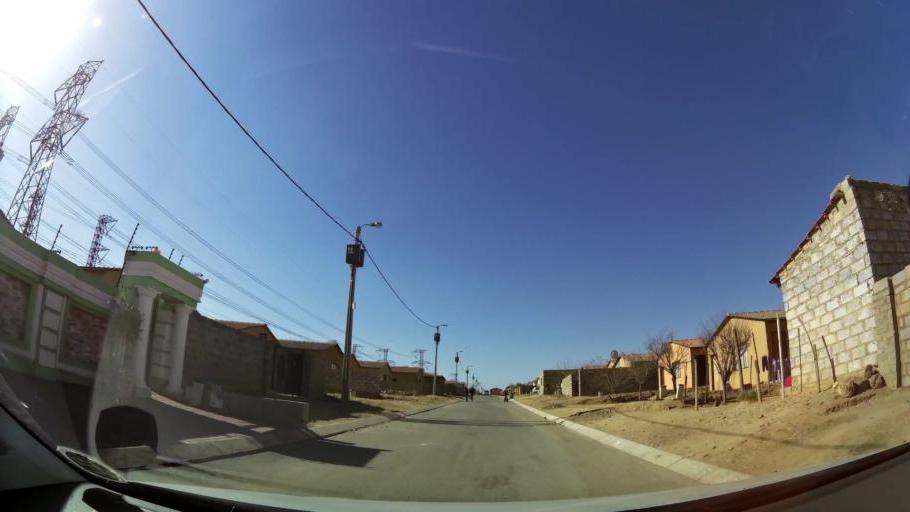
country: ZA
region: Gauteng
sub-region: Ekurhuleni Metropolitan Municipality
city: Tembisa
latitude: -26.0337
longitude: 28.2185
